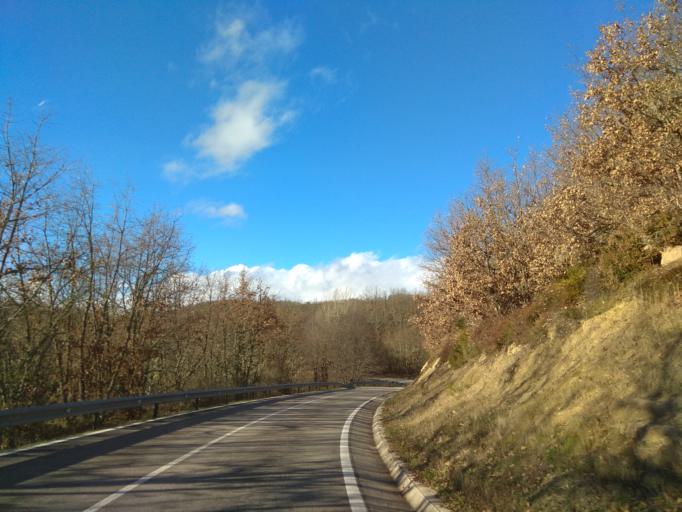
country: ES
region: Cantabria
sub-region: Provincia de Cantabria
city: San Martin de Elines
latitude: 42.9010
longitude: -3.8757
